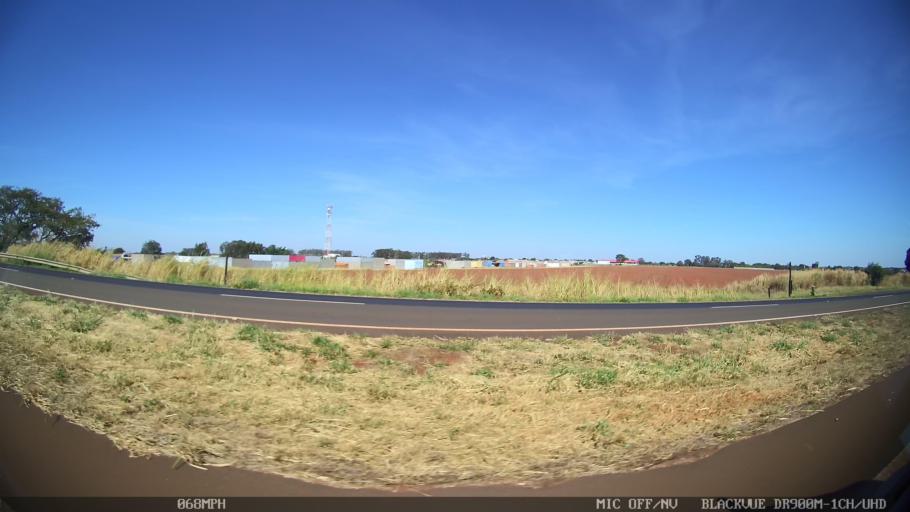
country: BR
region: Sao Paulo
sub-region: Barretos
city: Barretos
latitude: -20.5165
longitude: -48.5705
